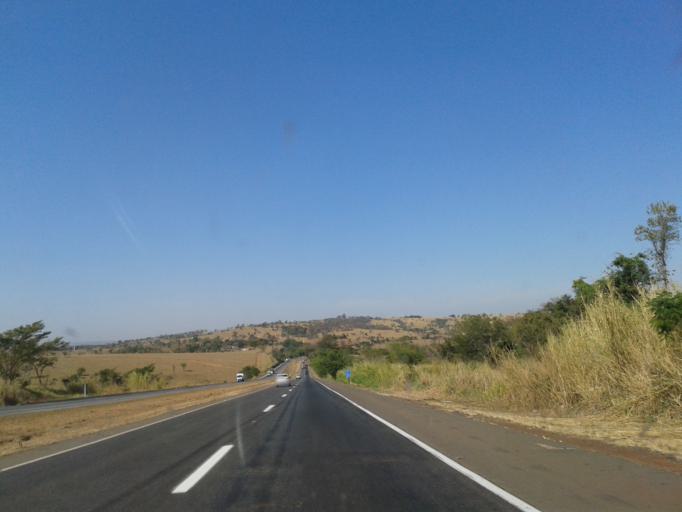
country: BR
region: Goias
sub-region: Piracanjuba
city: Piracanjuba
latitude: -17.1923
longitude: -49.2090
